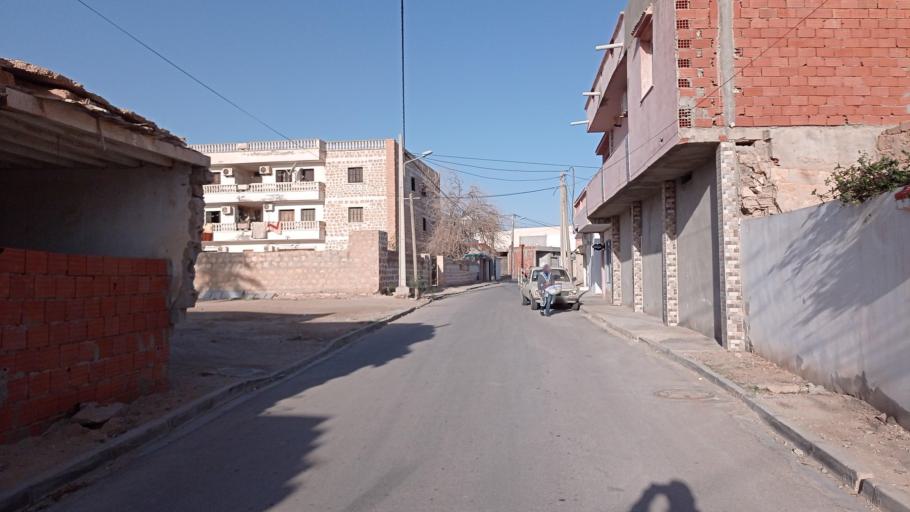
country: TN
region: Qabis
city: Gabes
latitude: 33.8553
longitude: 10.1199
